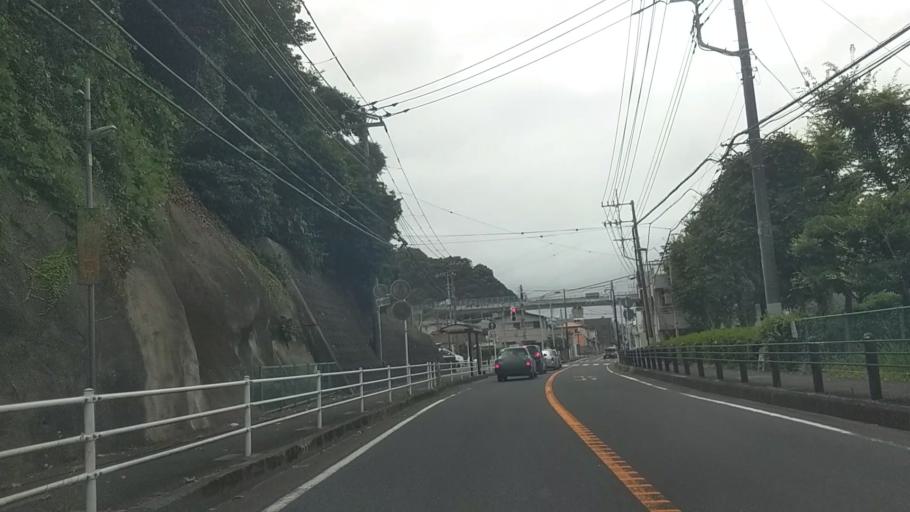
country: JP
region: Kanagawa
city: Yokosuka
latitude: 35.2597
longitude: 139.7129
